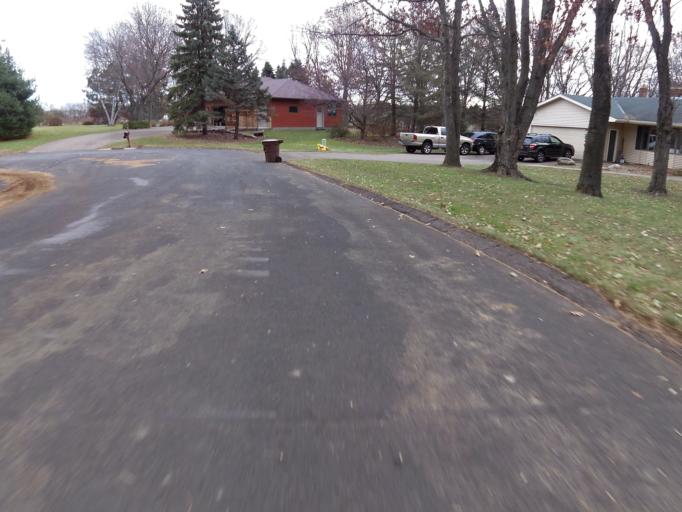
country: US
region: Minnesota
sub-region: Washington County
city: Lake Elmo
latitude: 44.9845
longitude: -92.8690
